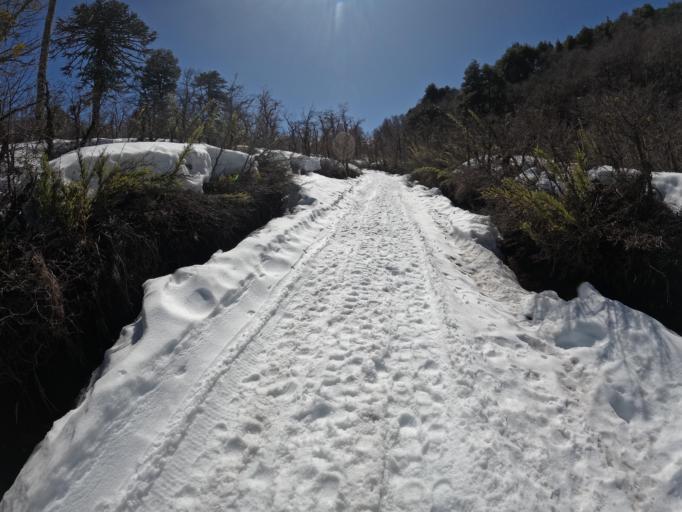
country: CL
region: Araucania
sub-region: Provincia de Cautin
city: Vilcun
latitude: -38.6626
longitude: -71.6189
